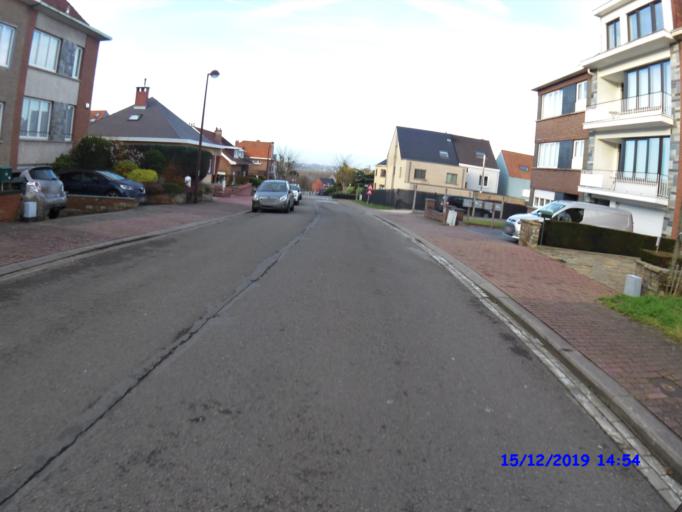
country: BE
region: Flanders
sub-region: Provincie Vlaams-Brabant
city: Drogenbos
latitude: 50.7703
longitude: 4.3172
